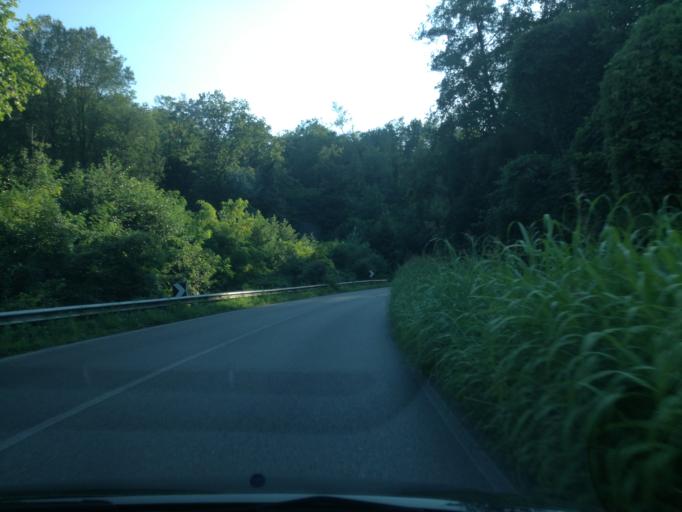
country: IT
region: Lombardy
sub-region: Provincia di Lecco
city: Imbersago
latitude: 45.6993
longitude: 9.4473
